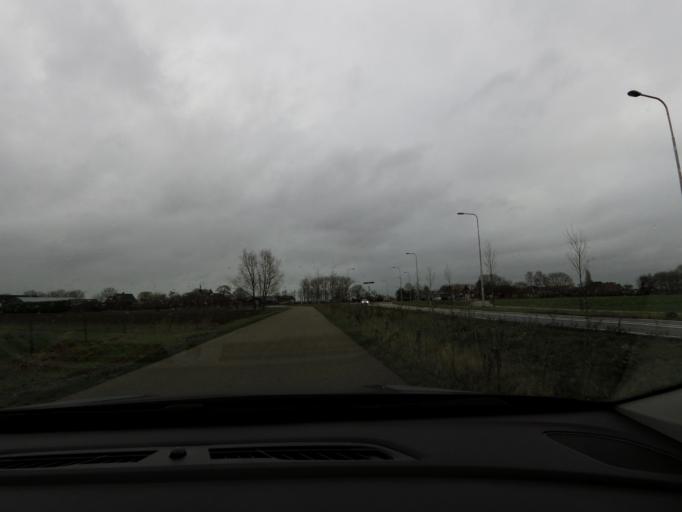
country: NL
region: North Brabant
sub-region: Gemeente Woudrichem
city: Almkerk
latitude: 51.7300
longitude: 5.0018
